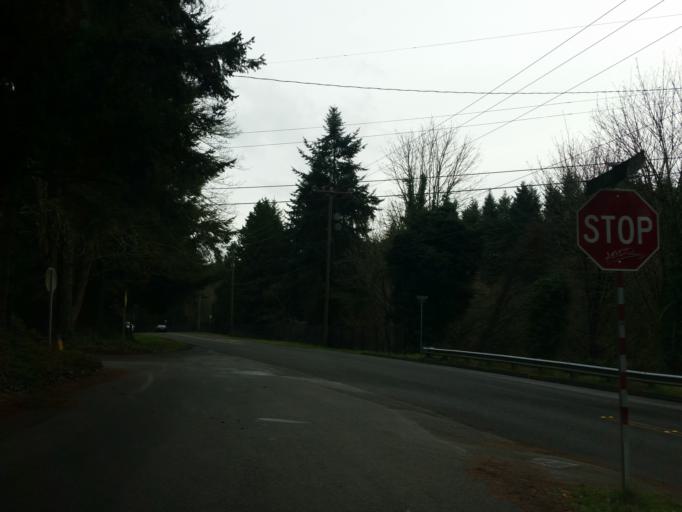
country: US
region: Washington
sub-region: King County
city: Shoreline
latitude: 47.7528
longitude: -122.3601
